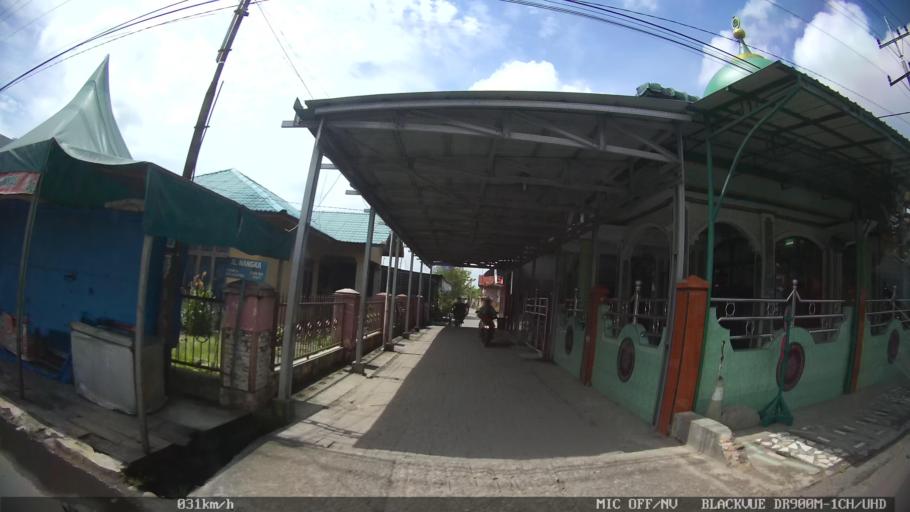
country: ID
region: North Sumatra
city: Percut
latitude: 3.6070
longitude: 98.7827
